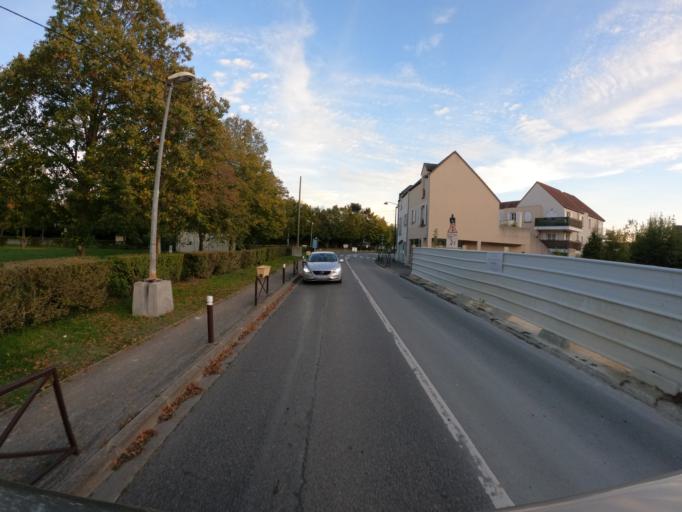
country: FR
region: Ile-de-France
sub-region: Departement de Seine-et-Marne
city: Emerainville
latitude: 48.8132
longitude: 2.6224
